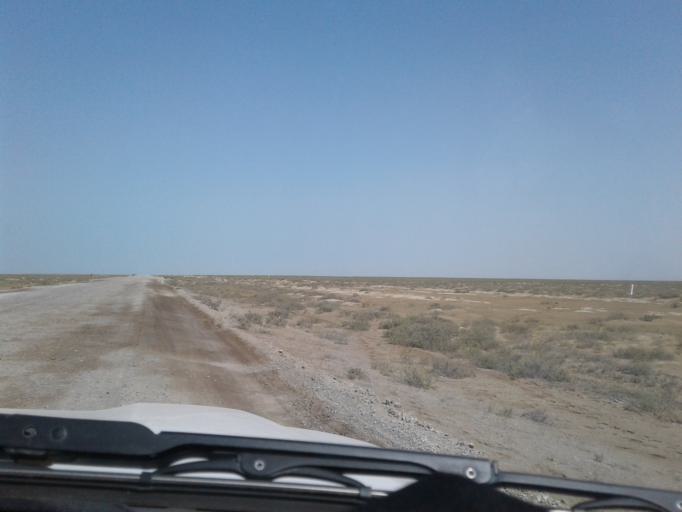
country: IR
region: Golestan
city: Gomishan
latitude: 37.8976
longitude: 53.8657
